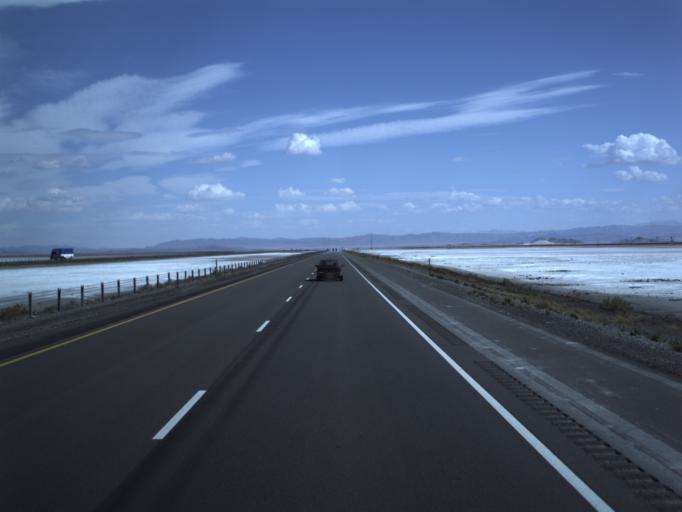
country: US
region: Utah
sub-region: Tooele County
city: Wendover
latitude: 40.7286
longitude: -113.4025
